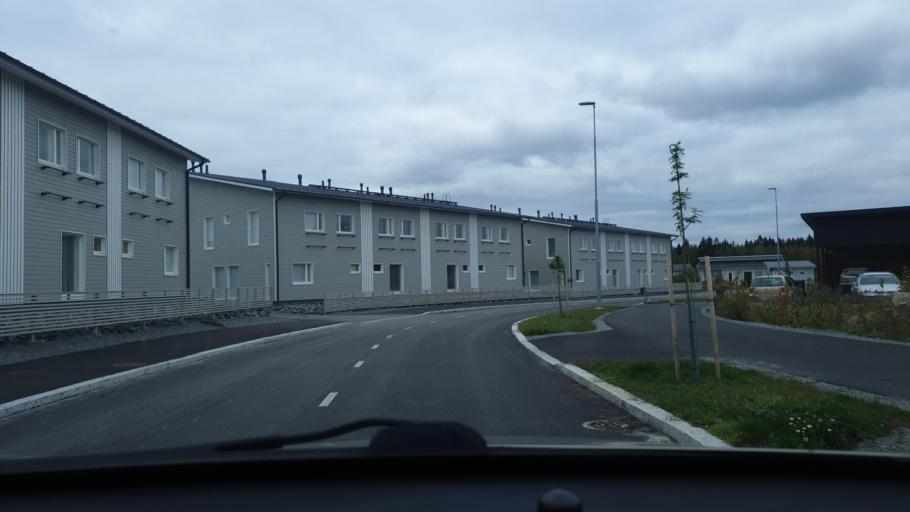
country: FI
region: Ostrobothnia
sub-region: Vaasa
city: Korsholm
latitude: 63.1292
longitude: 21.6510
